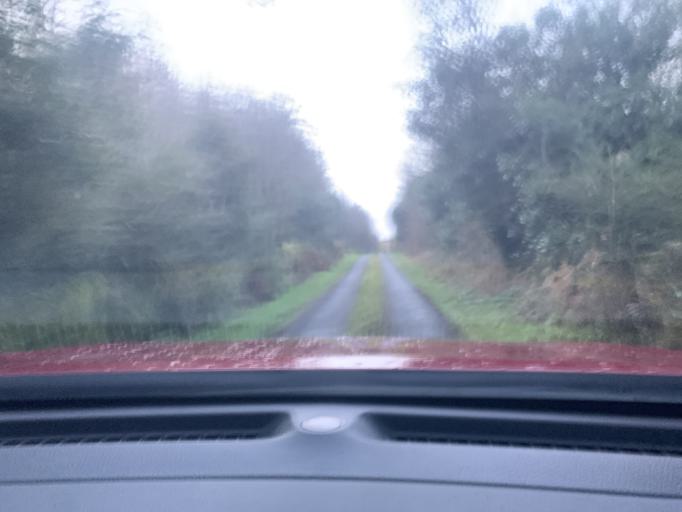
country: IE
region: Connaught
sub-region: Sligo
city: Ballymote
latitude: 53.9890
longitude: -8.4440
